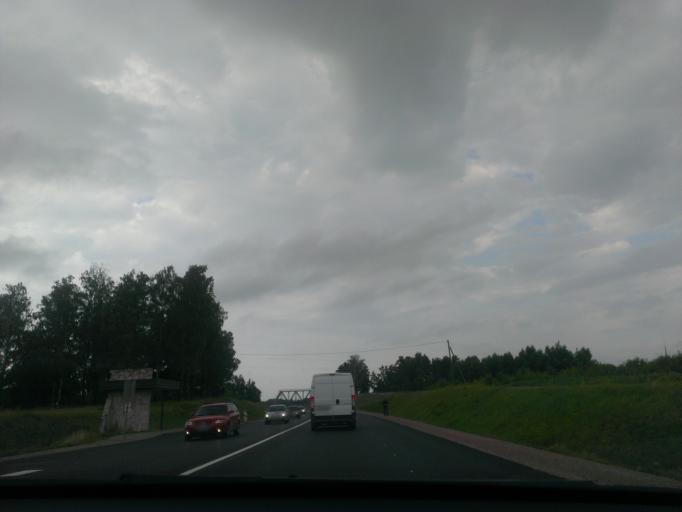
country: LV
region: Lecava
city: Iecava
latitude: 56.6279
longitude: 24.2218
